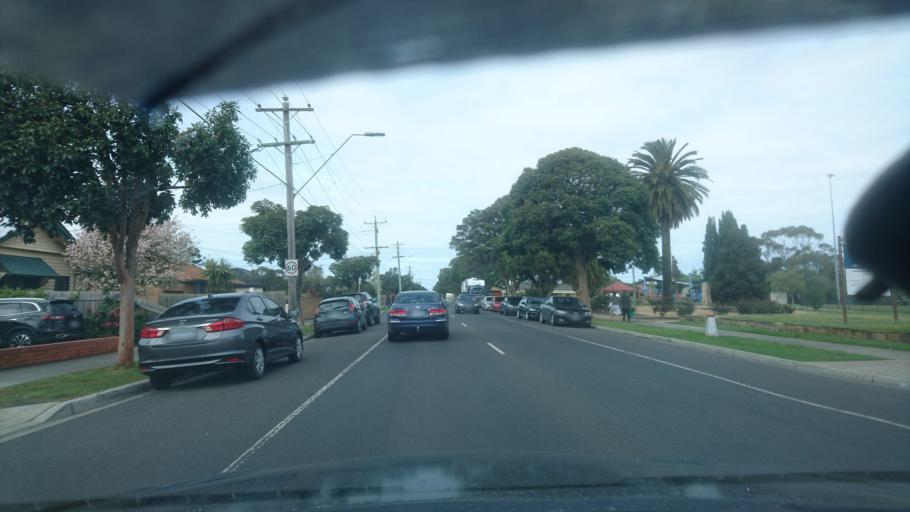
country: AU
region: Victoria
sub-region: Glen Eira
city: Carnegie
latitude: -37.8946
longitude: 145.0560
